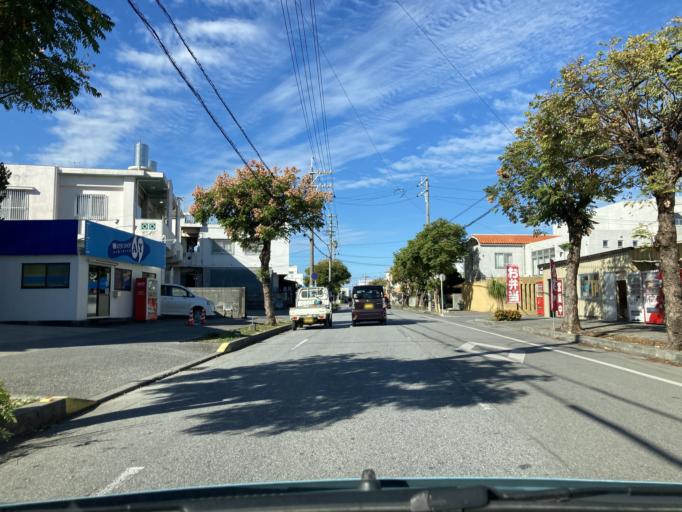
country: JP
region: Okinawa
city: Okinawa
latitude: 26.3705
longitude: 127.7522
